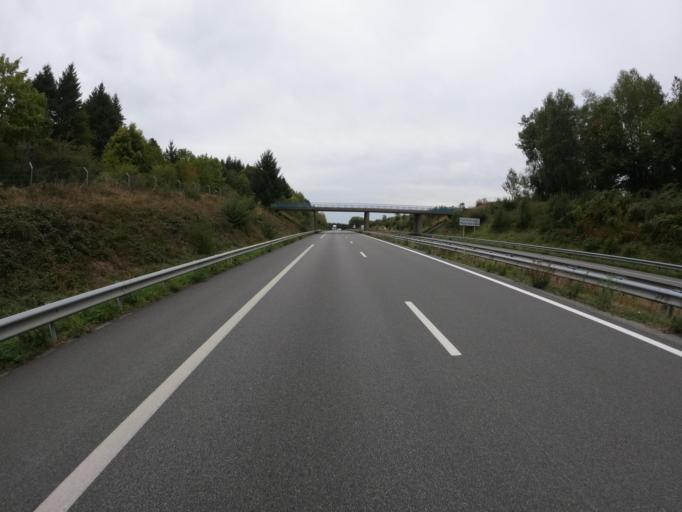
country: FR
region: Limousin
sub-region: Departement de la Creuse
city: Saint-Sulpice-le-Gueretois
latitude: 46.1925
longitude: 1.8032
